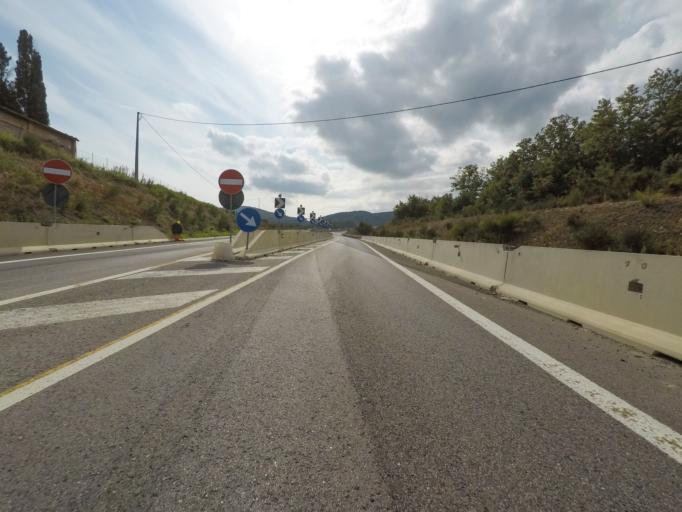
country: IT
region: Tuscany
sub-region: Provincia di Siena
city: Murlo
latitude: 43.1197
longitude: 11.2968
